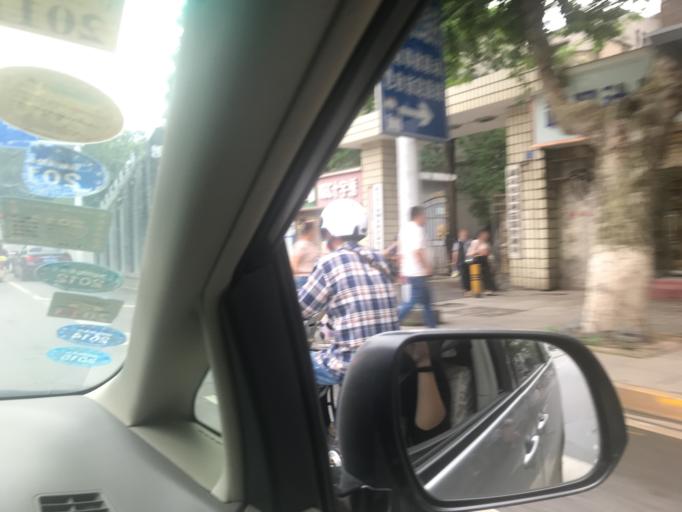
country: CN
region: Hubei
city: Wuhan
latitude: 30.5522
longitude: 114.2639
